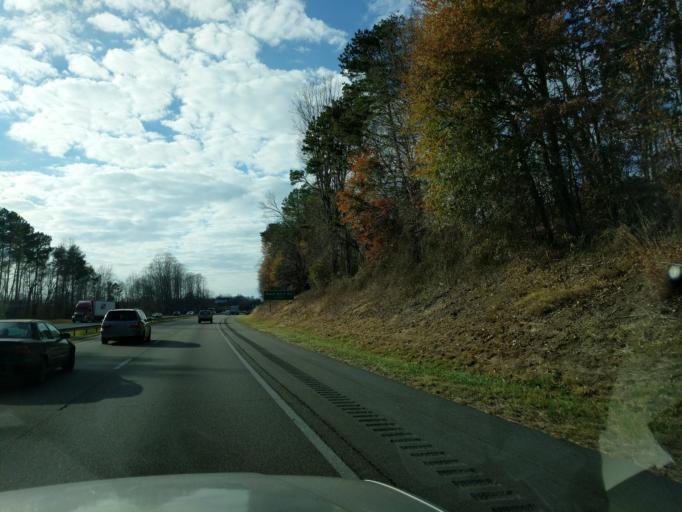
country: US
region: North Carolina
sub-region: Catawba County
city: Claremont
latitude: 35.7210
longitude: -81.1702
